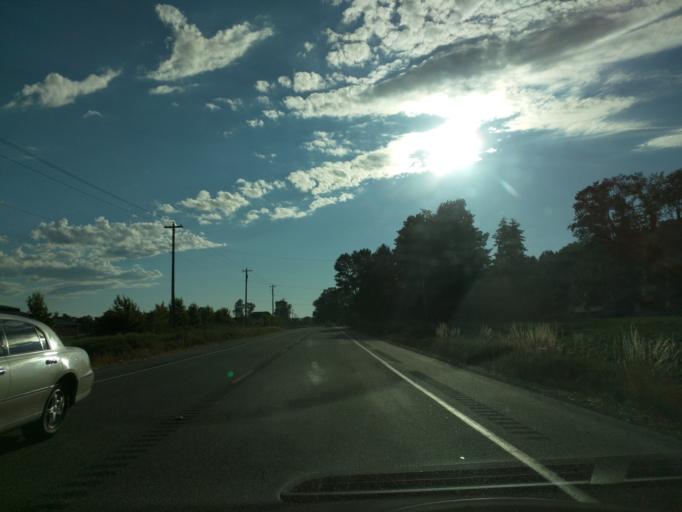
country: US
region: Washington
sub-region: Snohomish County
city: Smokey Point
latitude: 48.1886
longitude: -122.1679
